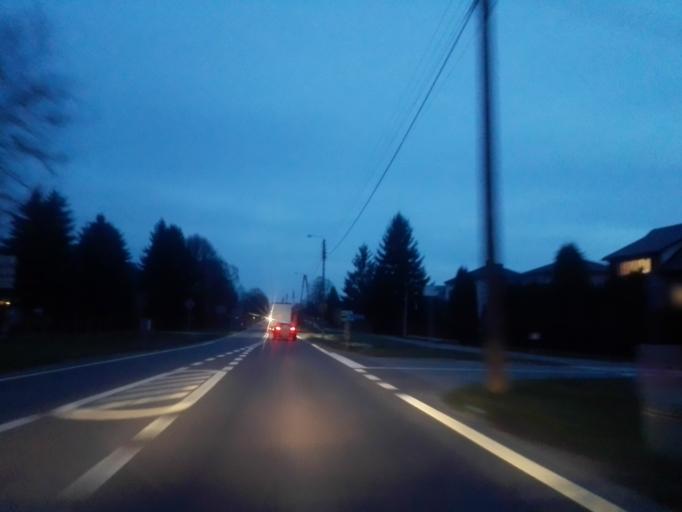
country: PL
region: Podlasie
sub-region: Lomza
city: Lomza
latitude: 53.1446
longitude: 22.0454
